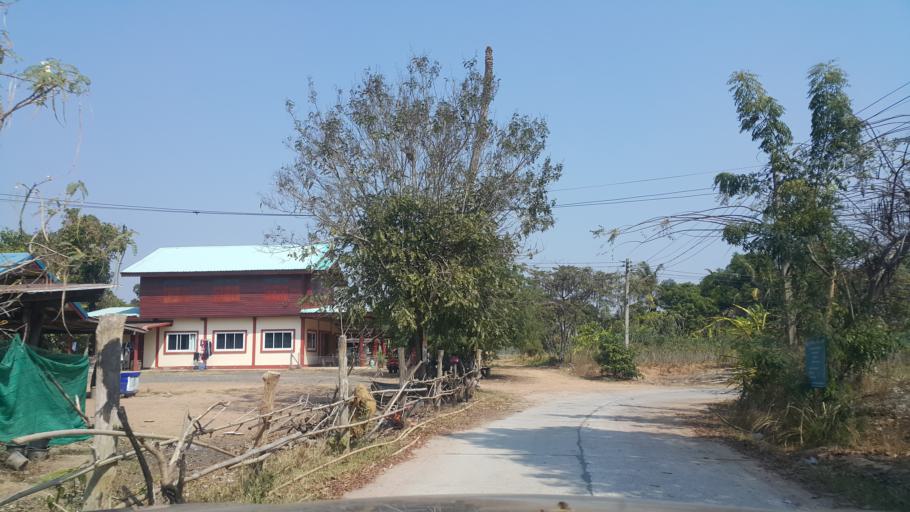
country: TH
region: Buriram
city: Krasang
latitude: 15.0970
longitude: 103.3716
